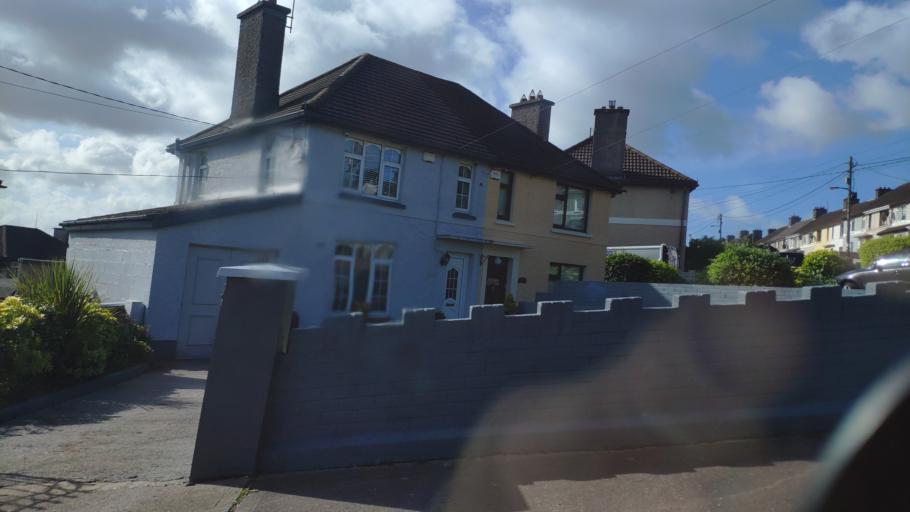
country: IE
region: Munster
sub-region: County Cork
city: Cork
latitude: 51.9165
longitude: -8.4803
